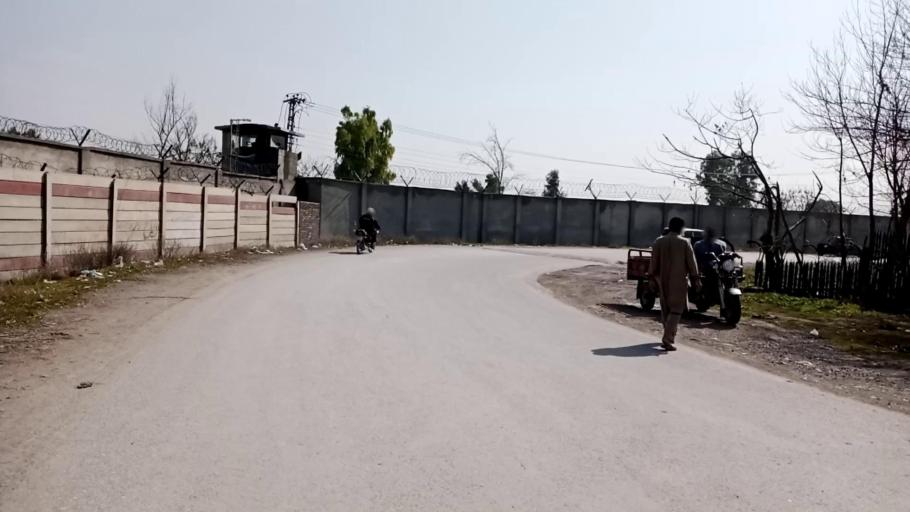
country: PK
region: Khyber Pakhtunkhwa
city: Peshawar
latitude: 33.9941
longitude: 71.5105
